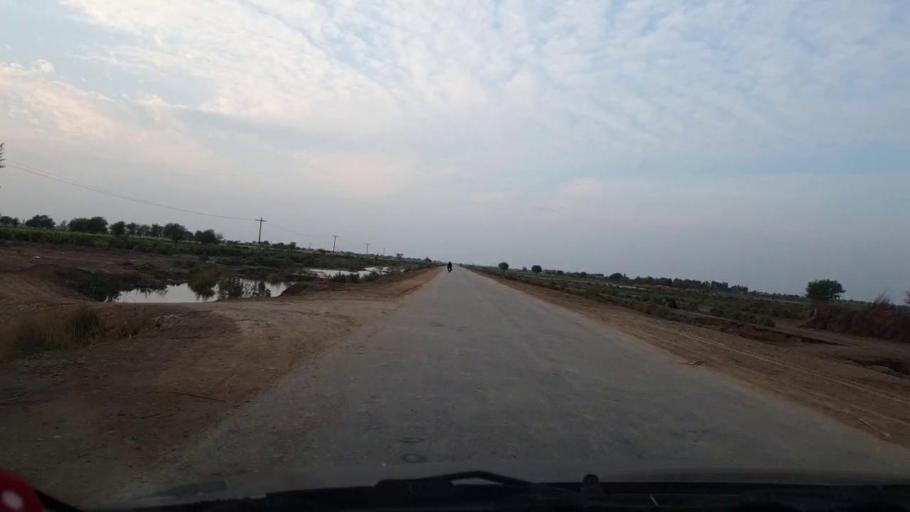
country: PK
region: Sindh
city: Jhol
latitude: 25.9940
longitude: 68.8529
